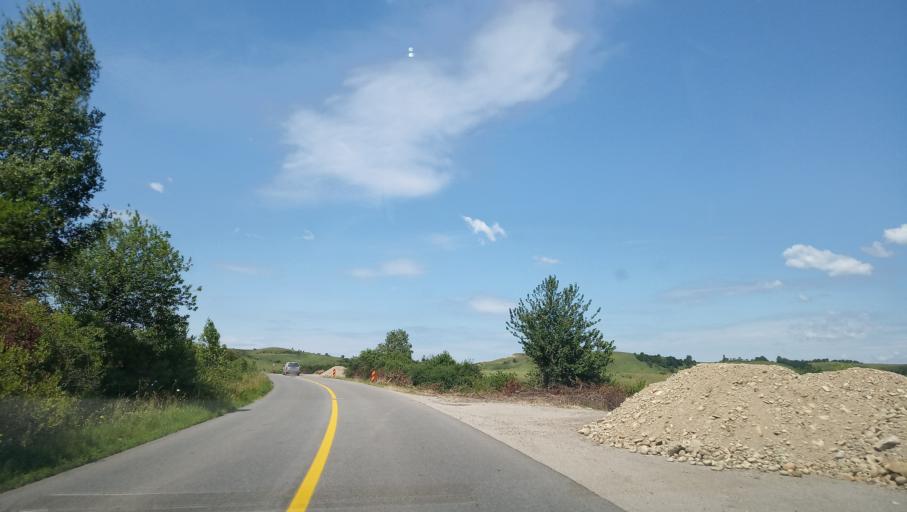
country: RO
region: Hunedoara
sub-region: Comuna Calan
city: Calan
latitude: 45.7318
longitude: 22.9487
